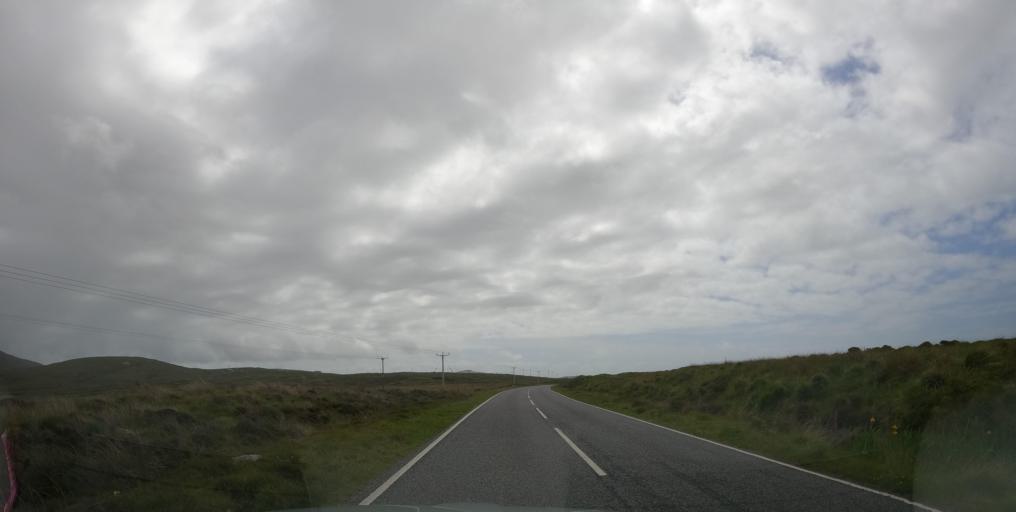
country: GB
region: Scotland
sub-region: Eilean Siar
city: Isle of South Uist
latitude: 57.2730
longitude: -7.3653
